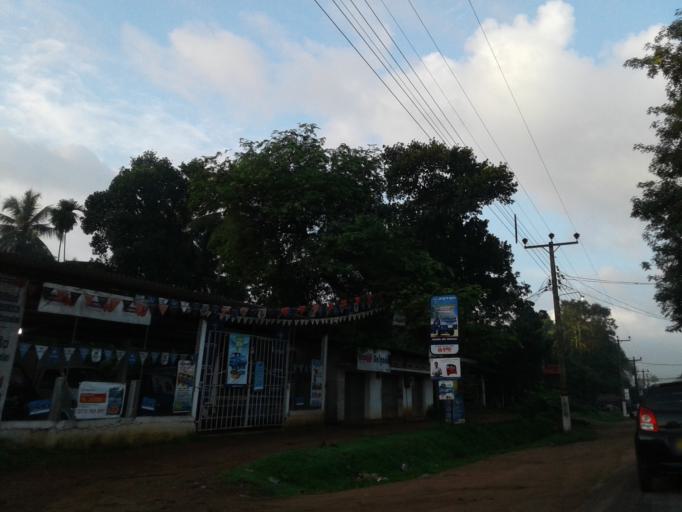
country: LK
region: Western
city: Kelaniya
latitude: 6.9785
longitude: 80.0081
